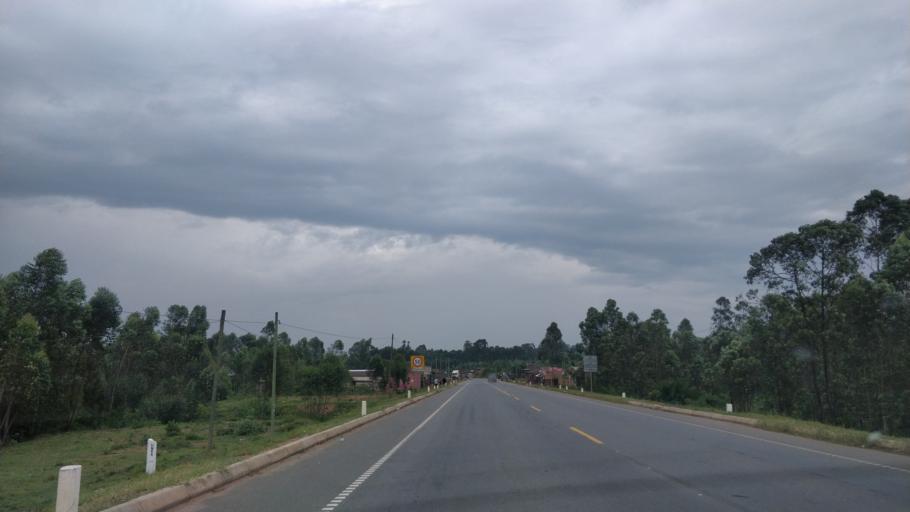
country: UG
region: Western Region
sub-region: Sheema District
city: Kibingo
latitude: -0.6686
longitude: 30.4418
